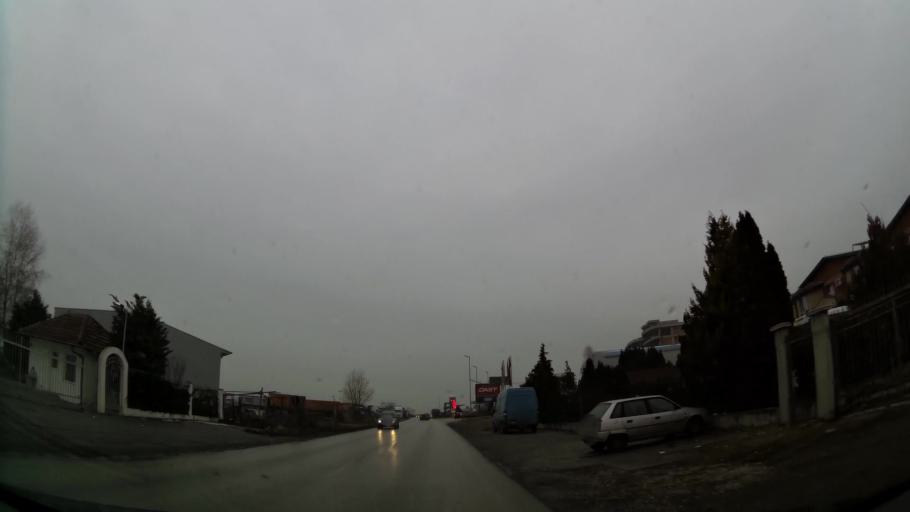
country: MK
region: Suto Orizari
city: Suto Orizare
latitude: 42.0427
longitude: 21.3917
